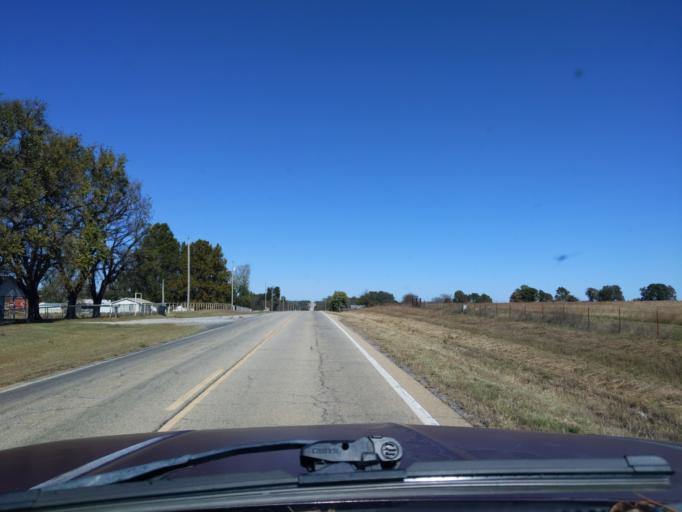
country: US
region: Oklahoma
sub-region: Creek County
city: Bristow
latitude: 35.7203
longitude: -96.3872
